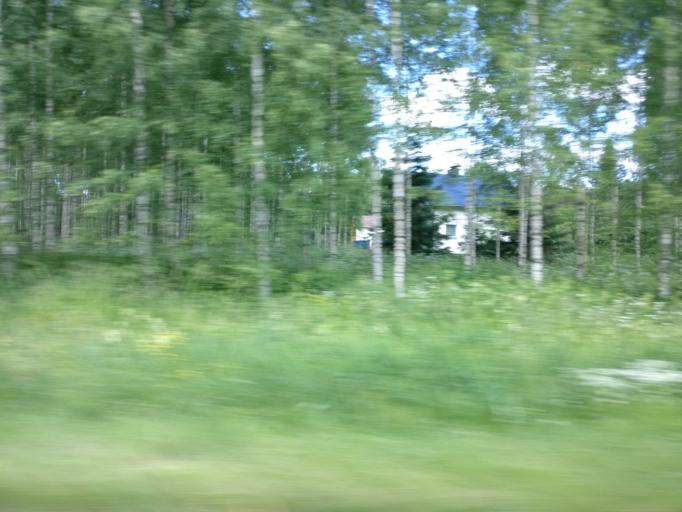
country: FI
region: Southern Savonia
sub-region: Savonlinna
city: Kerimaeki
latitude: 61.8293
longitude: 29.2342
